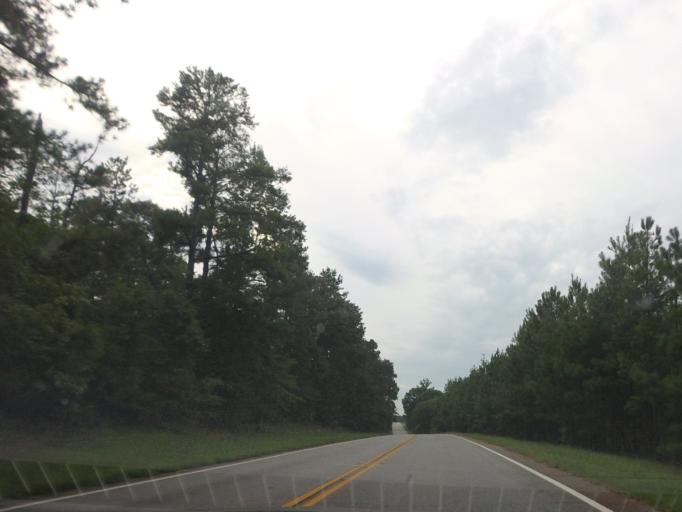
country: US
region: Georgia
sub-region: Twiggs County
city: Jeffersonville
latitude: 32.7160
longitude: -83.3911
